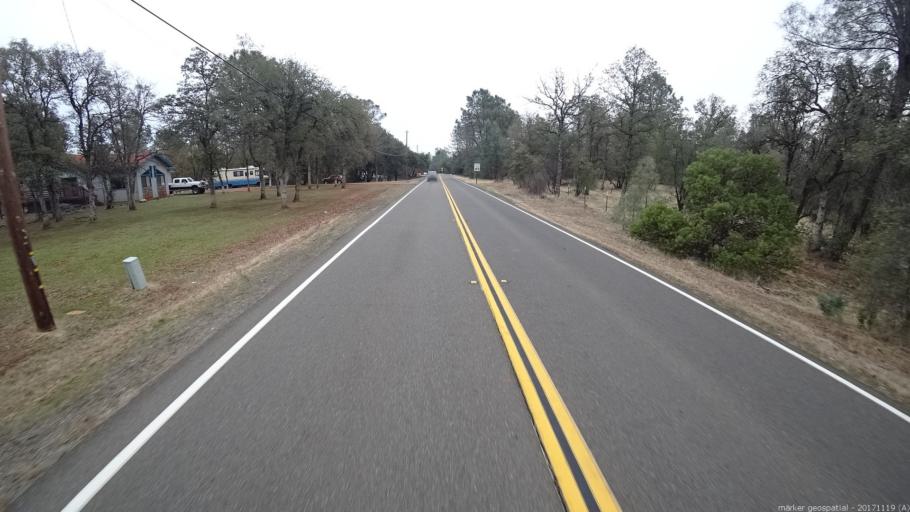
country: US
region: California
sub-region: Shasta County
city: Redding
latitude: 40.4900
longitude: -122.4035
